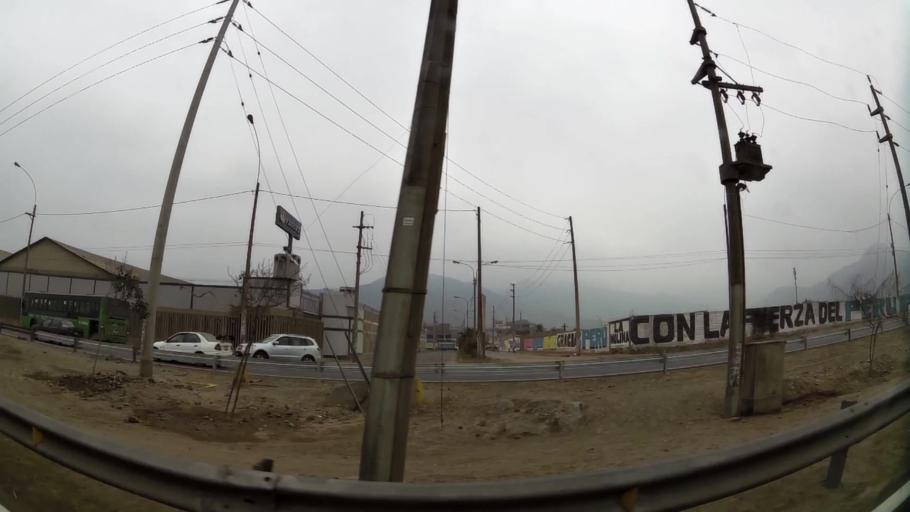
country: PE
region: Lima
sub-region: Lima
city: Vitarte
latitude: -12.0252
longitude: -76.9661
